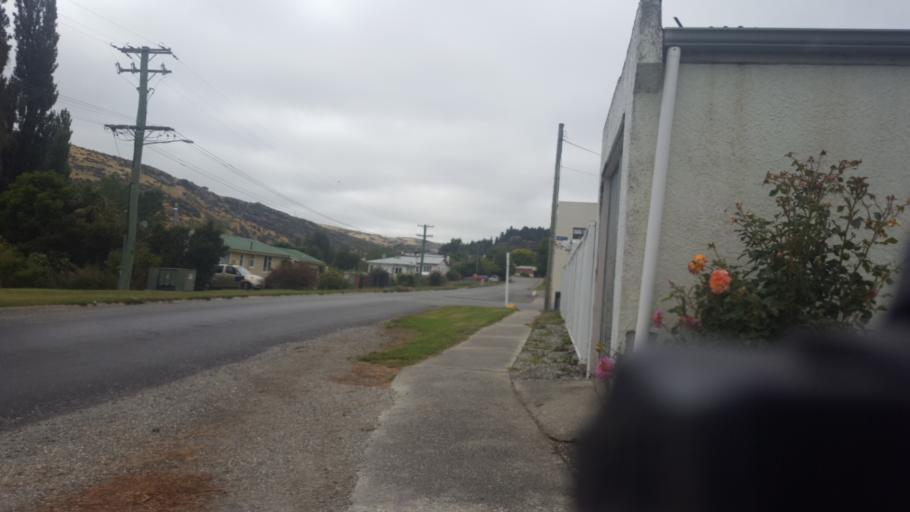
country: NZ
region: Otago
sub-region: Queenstown-Lakes District
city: Kingston
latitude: -45.5400
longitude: 169.3161
